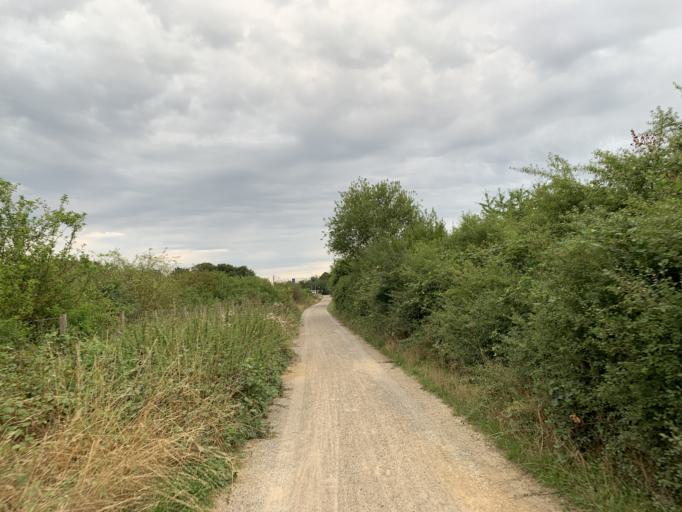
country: DE
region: North Rhine-Westphalia
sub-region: Regierungsbezirk Koln
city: Dueren
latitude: 50.7853
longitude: 6.4848
